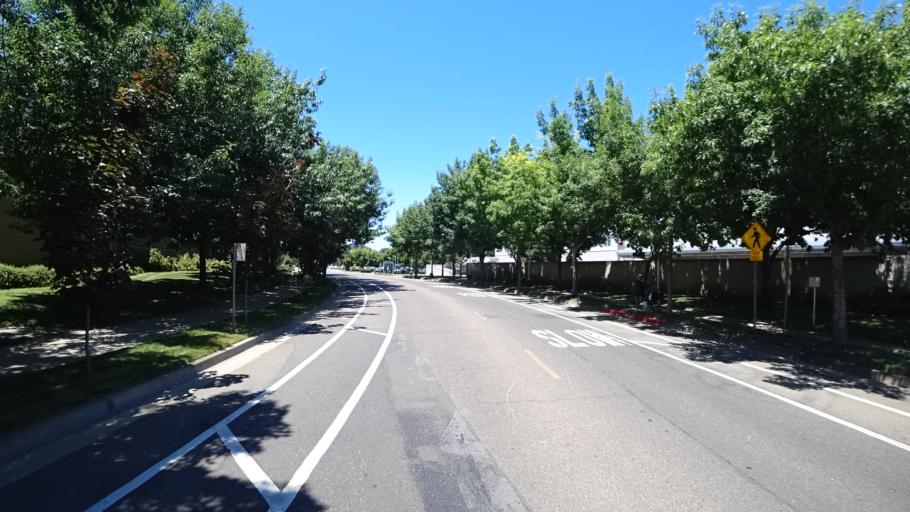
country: US
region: California
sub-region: Sacramento County
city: Sacramento
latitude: 38.5509
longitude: -121.4491
